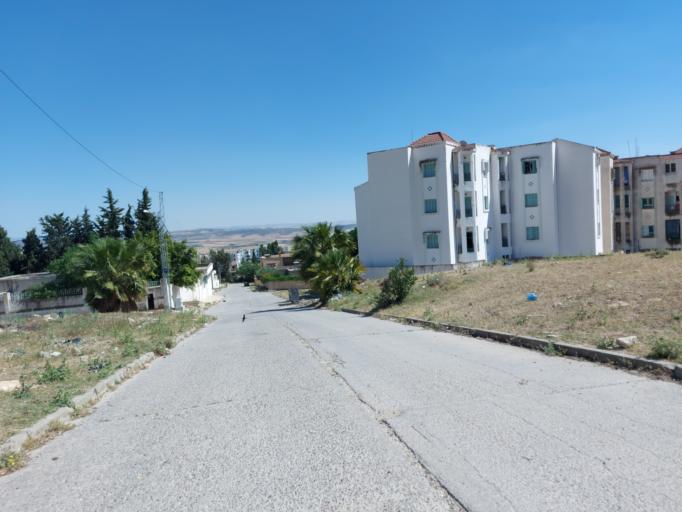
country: TN
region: Kef
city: El Kef
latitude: 36.1826
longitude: 8.7284
